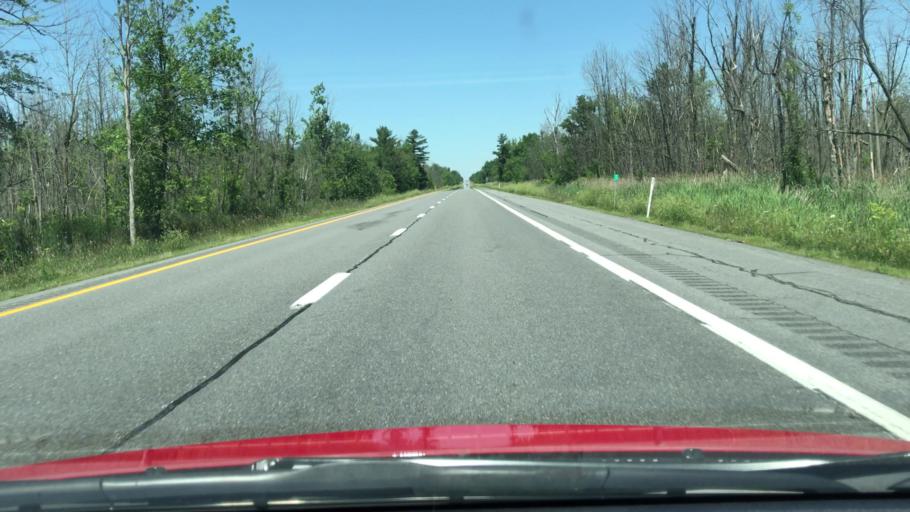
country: US
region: New York
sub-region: Clinton County
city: Champlain
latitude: 44.9388
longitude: -73.4470
